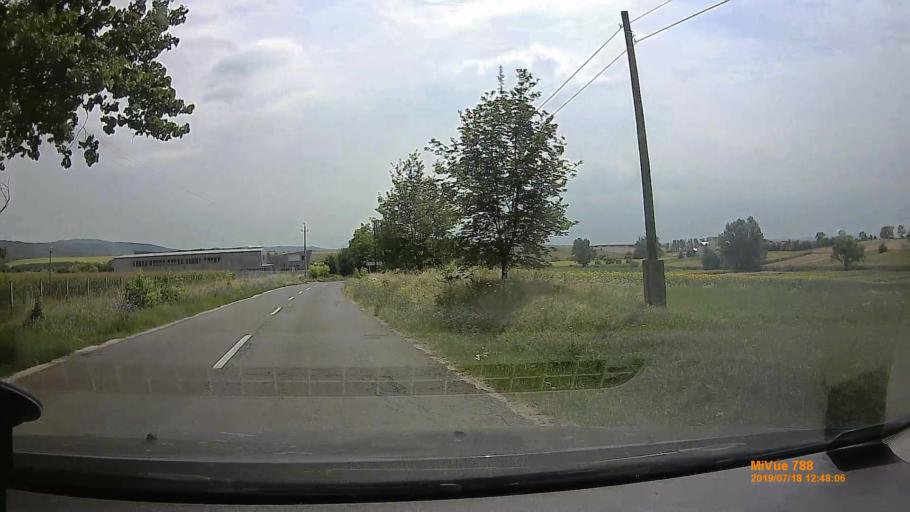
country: HU
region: Pest
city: Perbal
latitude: 47.5851
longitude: 18.7653
